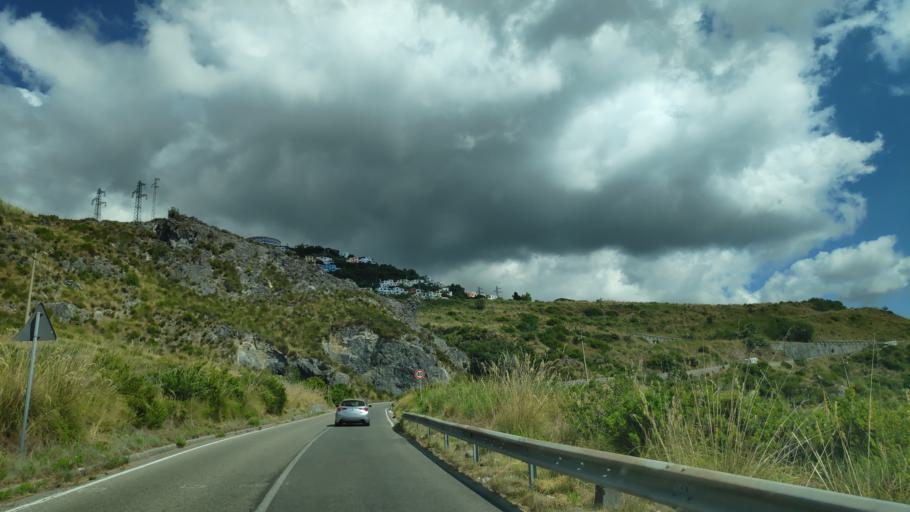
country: IT
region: Calabria
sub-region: Provincia di Cosenza
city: San Nicola Arcella
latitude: 39.8682
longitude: 15.7937
